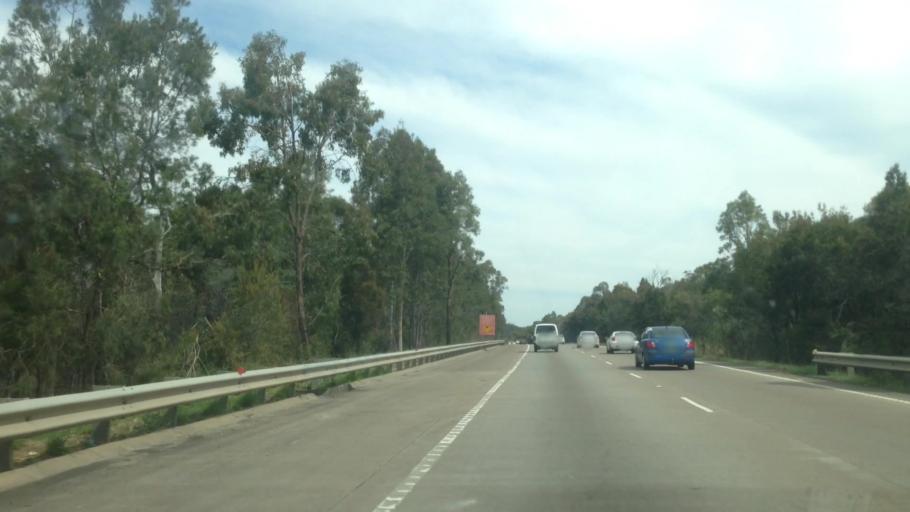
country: AU
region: New South Wales
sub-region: Lake Macquarie Shire
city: Fennell Bay
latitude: -32.9604
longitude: 151.5408
